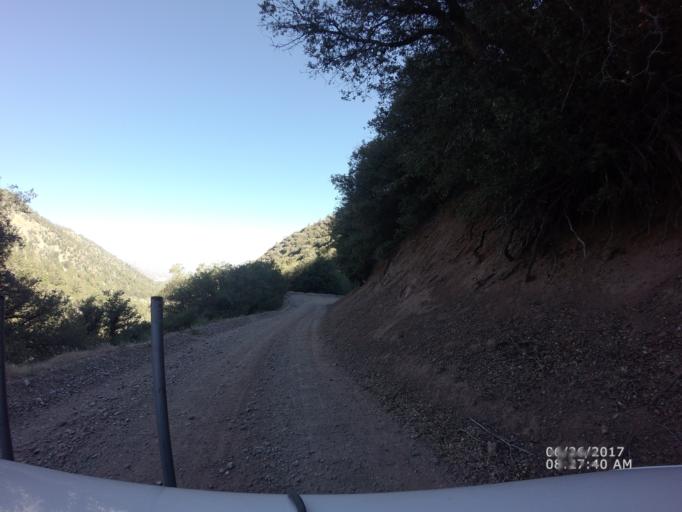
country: US
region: California
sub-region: San Bernardino County
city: Wrightwood
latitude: 34.3752
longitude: -117.7540
